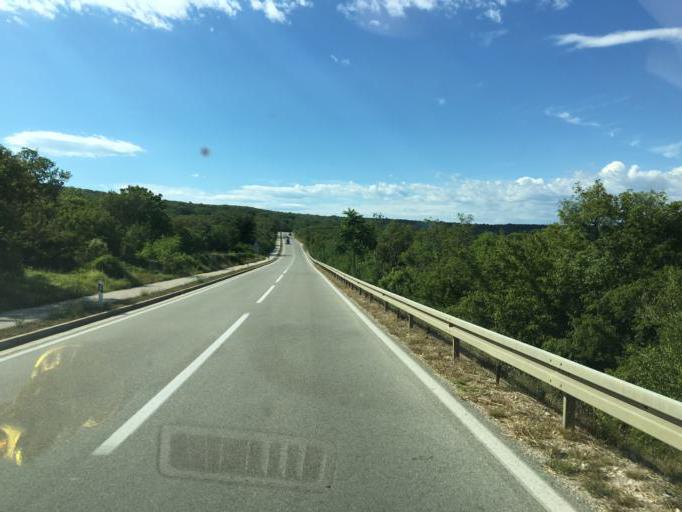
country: HR
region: Primorsko-Goranska
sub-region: Grad Krk
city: Krk
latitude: 45.0692
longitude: 14.5547
